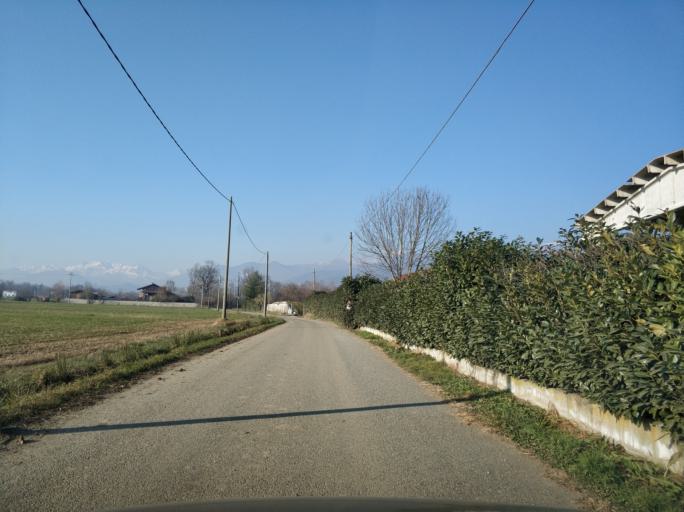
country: IT
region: Piedmont
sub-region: Provincia di Torino
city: Barbania
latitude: 45.3089
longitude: 7.6389
